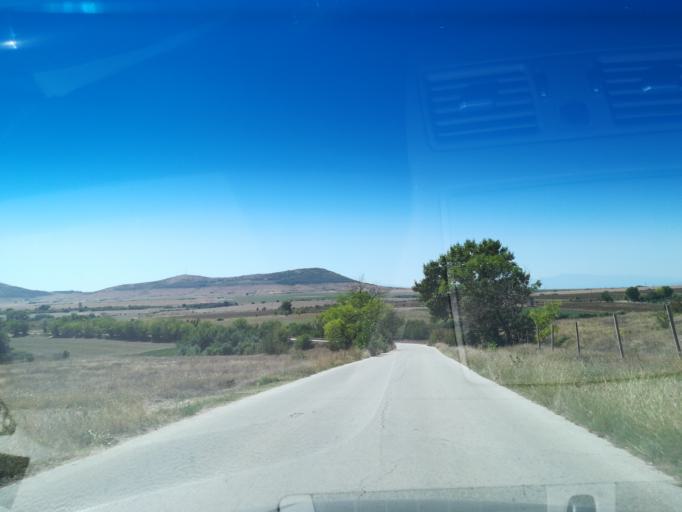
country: BG
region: Pazardzhik
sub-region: Obshtina Strelcha
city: Strelcha
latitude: 42.3592
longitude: 24.4011
